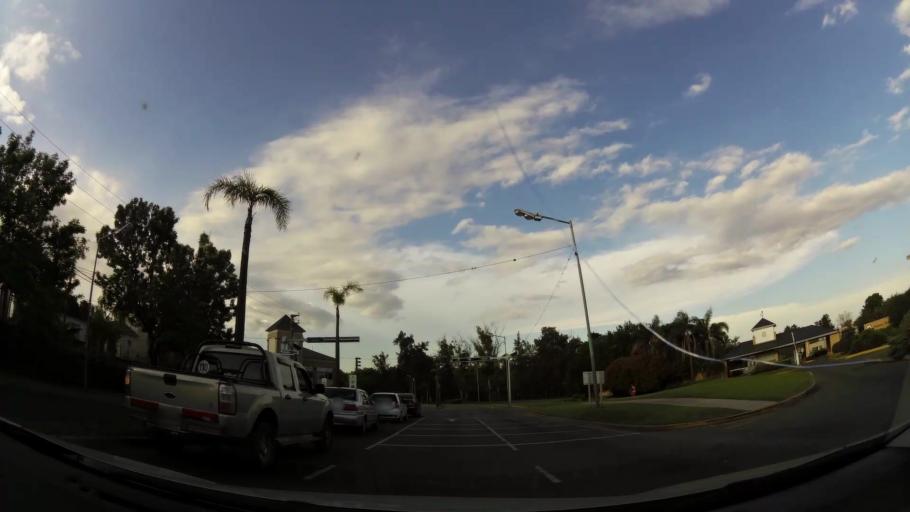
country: AR
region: Buenos Aires
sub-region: Partido de Tigre
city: Tigre
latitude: -34.4693
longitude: -58.6241
